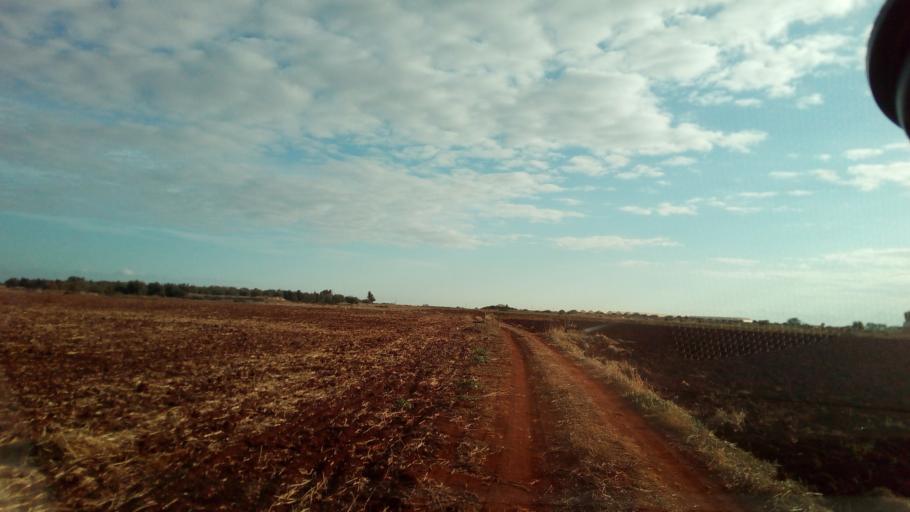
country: CY
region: Ammochostos
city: Liopetri
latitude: 35.0365
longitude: 33.8733
